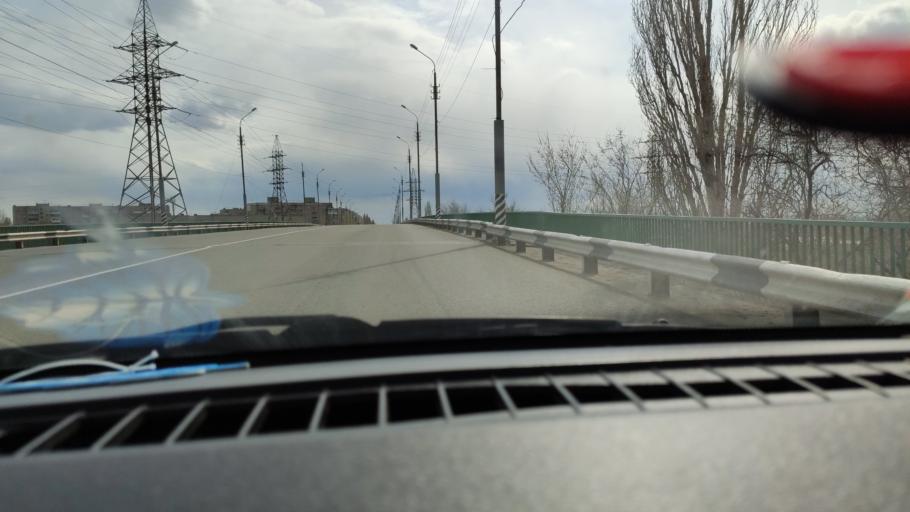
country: RU
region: Saratov
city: Privolzhskiy
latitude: 51.4145
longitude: 46.0438
